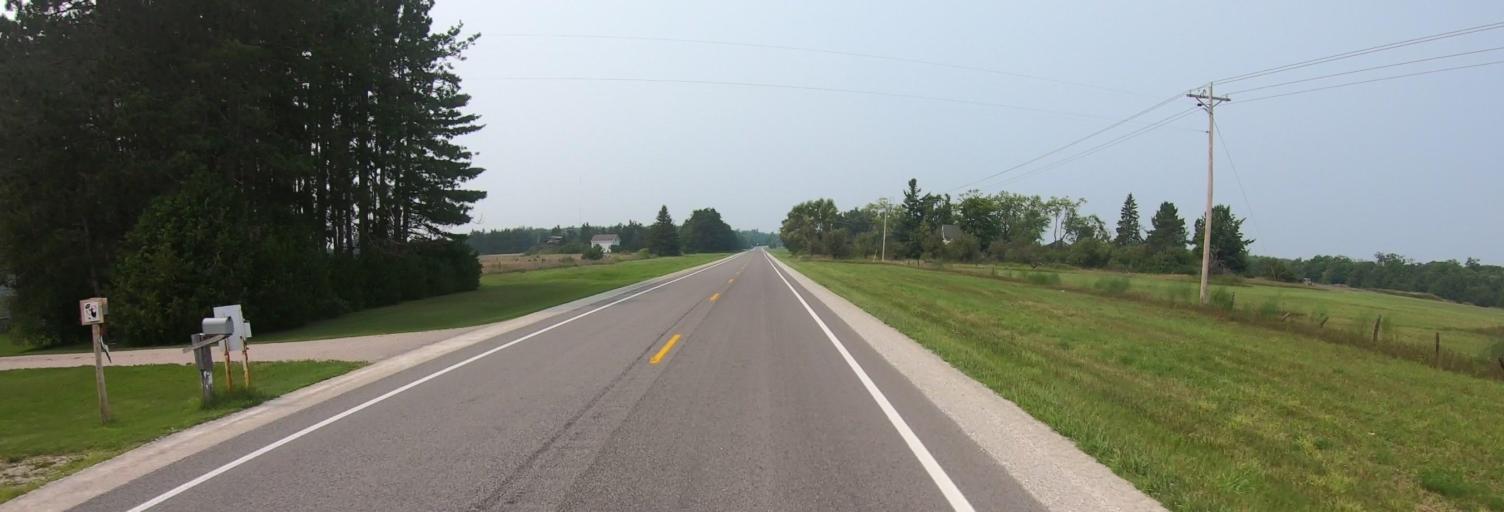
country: US
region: Michigan
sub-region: Chippewa County
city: Sault Ste. Marie
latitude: 46.0343
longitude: -84.0858
